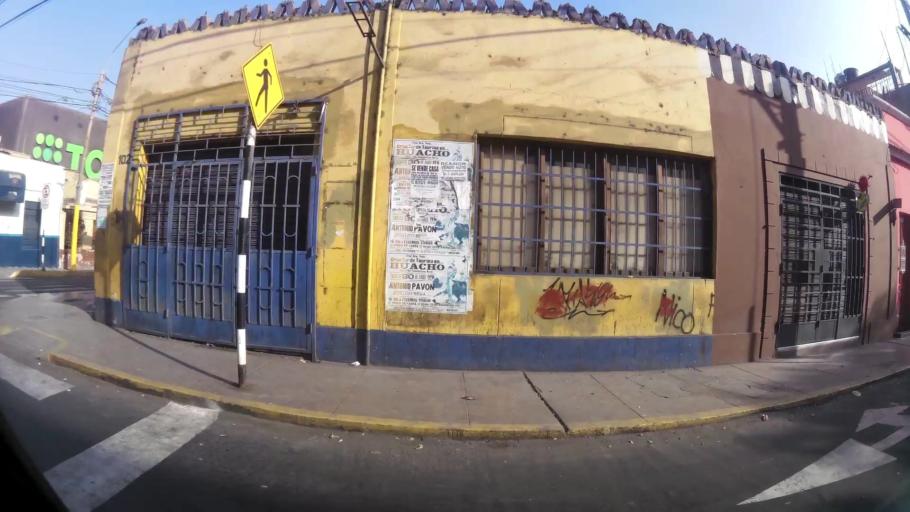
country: PE
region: Lima
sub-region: Huaura
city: Huacho
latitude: -11.1080
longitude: -77.6051
